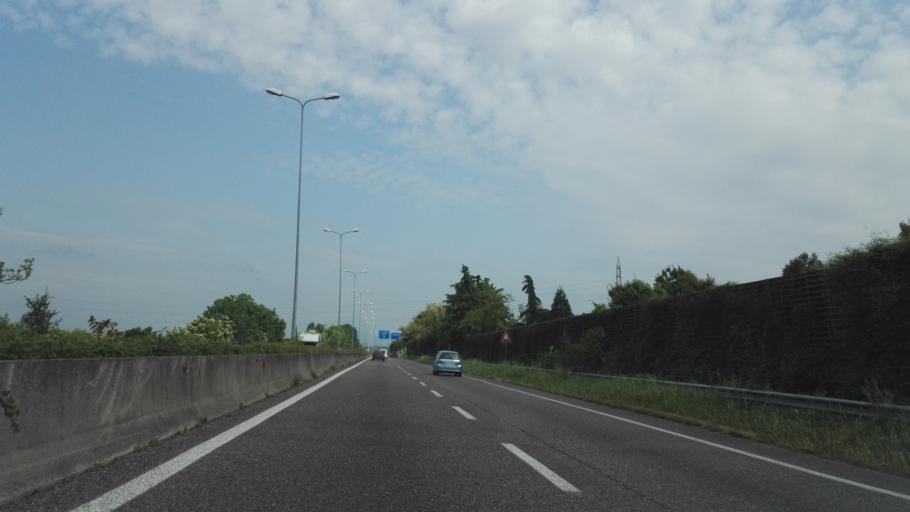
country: IT
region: Lombardy
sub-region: Provincia di Monza e Brianza
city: Cesano Maderno
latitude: 45.6344
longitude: 9.1607
